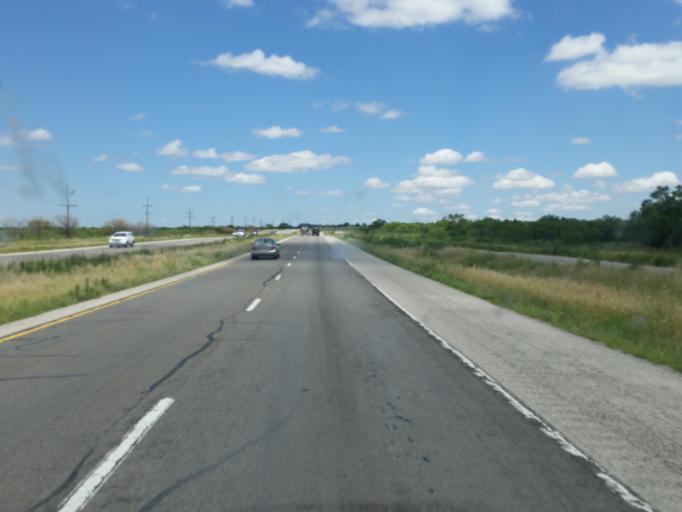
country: US
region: Texas
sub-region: Nolan County
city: Sweetwater
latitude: 32.4957
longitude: -100.2752
